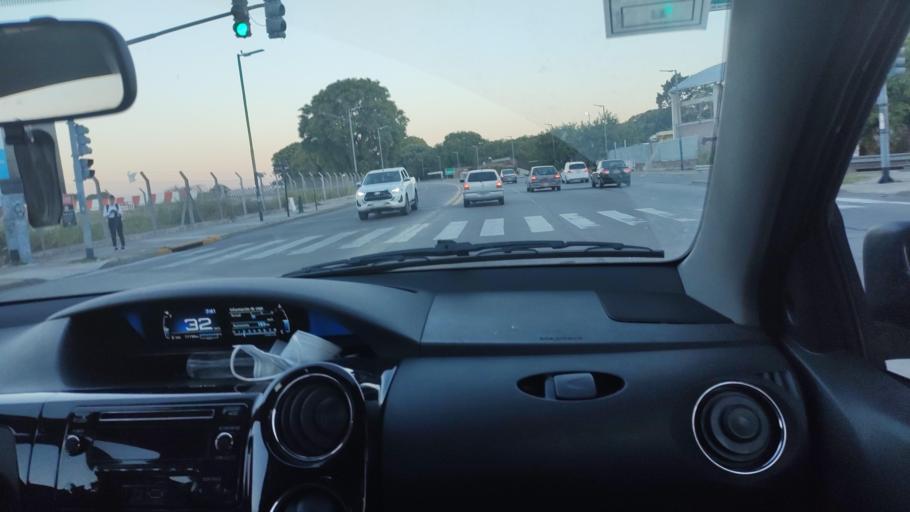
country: AR
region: Buenos Aires F.D.
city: Retiro
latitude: -34.5672
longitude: -58.4053
